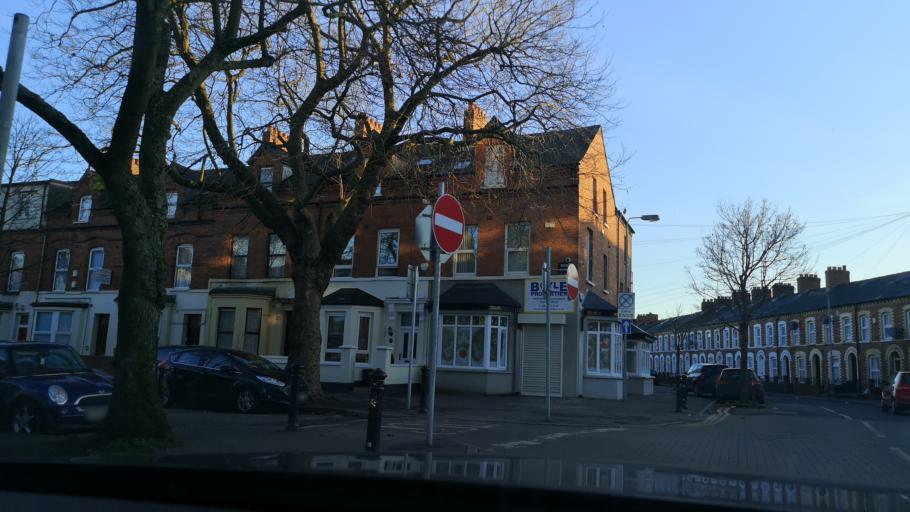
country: GB
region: Northern Ireland
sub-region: City of Belfast
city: Belfast
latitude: 54.5843
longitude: -5.9284
